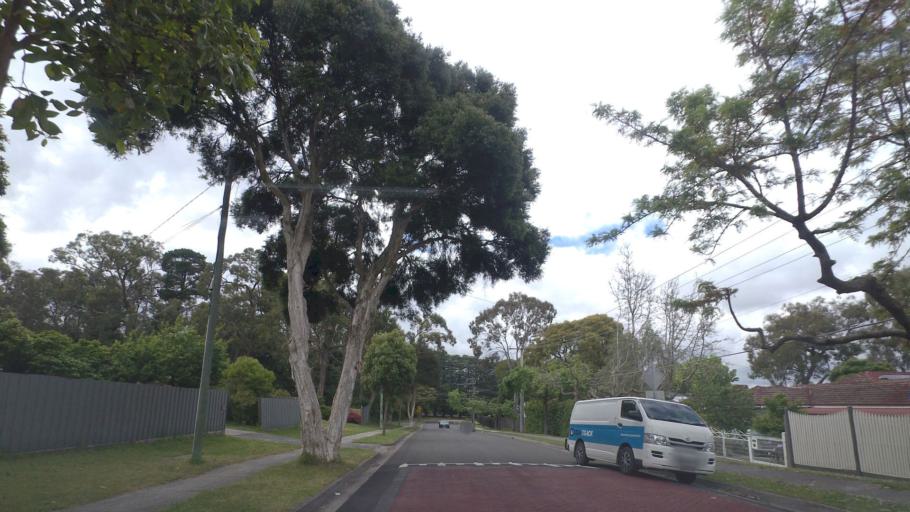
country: AU
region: Victoria
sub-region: Maroondah
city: Croydon South
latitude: -37.7974
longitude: 145.2684
